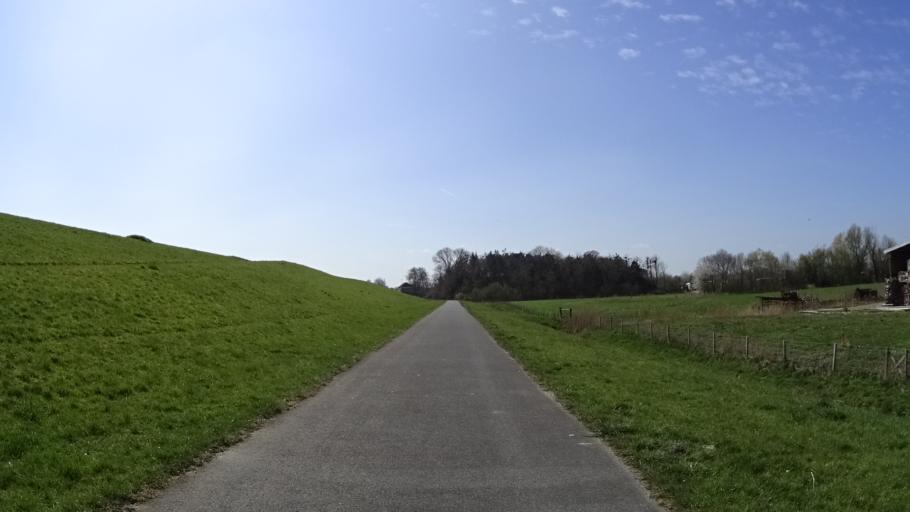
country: DE
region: Lower Saxony
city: Weener
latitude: 53.1738
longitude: 7.3707
